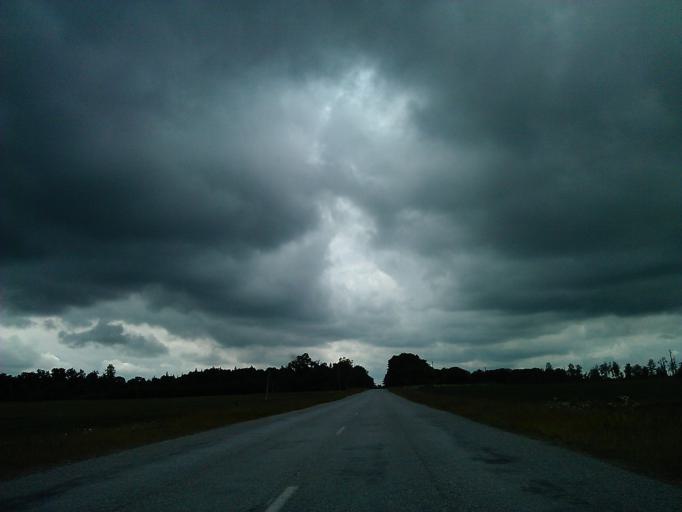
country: LV
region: Aizpute
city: Aizpute
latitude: 56.8194
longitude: 21.7290
